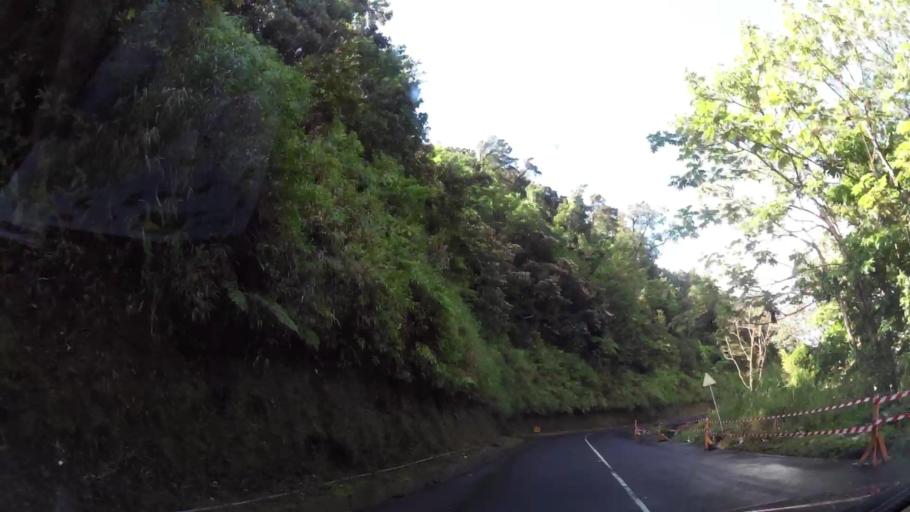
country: DM
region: Saint Paul
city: Pont Casse
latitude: 15.3729
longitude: -61.3454
